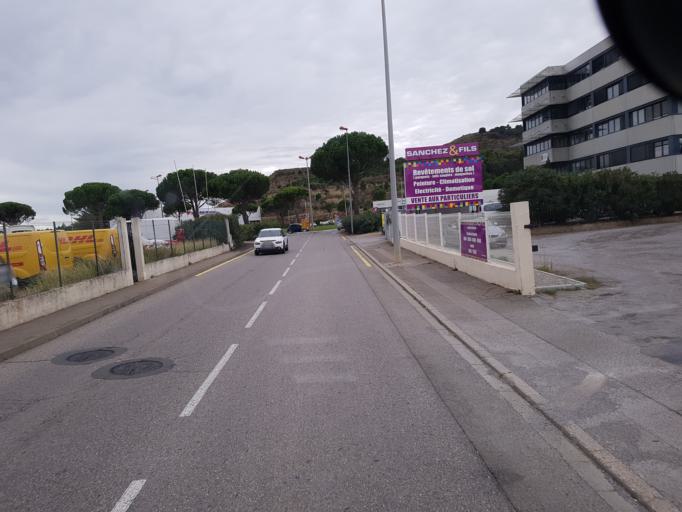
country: FR
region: Languedoc-Roussillon
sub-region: Departement de l'Aude
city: Narbonne
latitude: 43.1587
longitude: 2.9785
